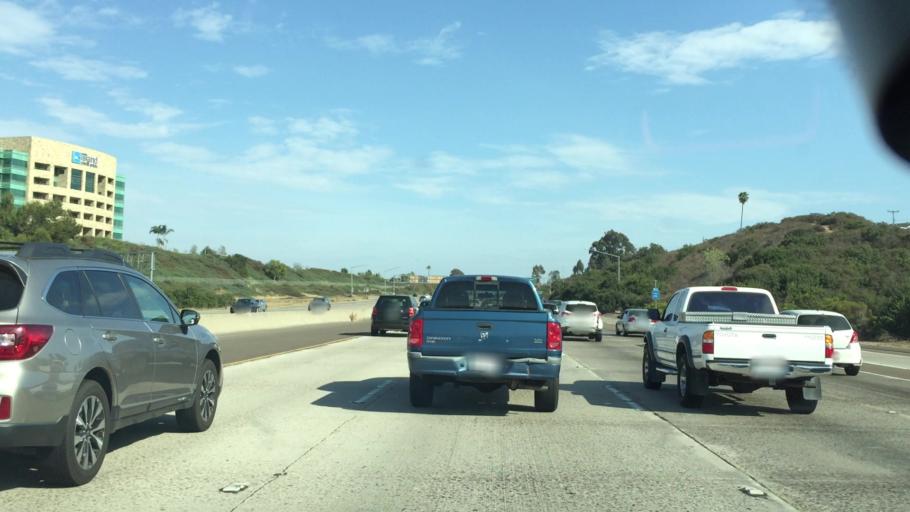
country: US
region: California
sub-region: San Diego County
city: La Jolla
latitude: 32.8450
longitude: -117.1767
